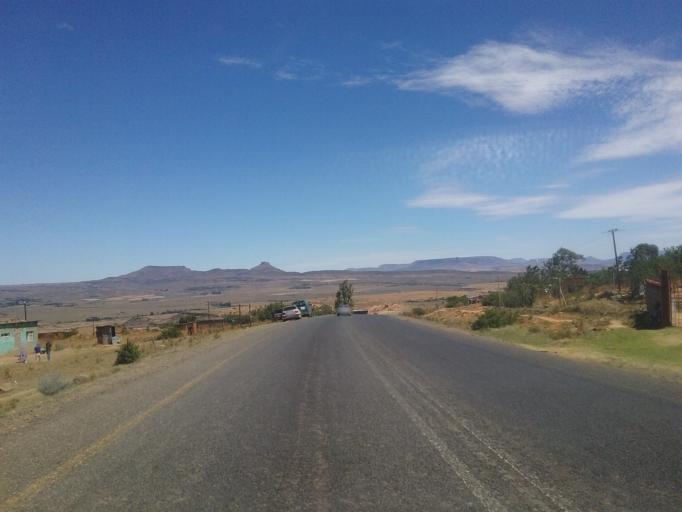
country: LS
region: Mohale's Hoek District
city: Mohale's Hoek
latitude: -30.2013
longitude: 27.4184
